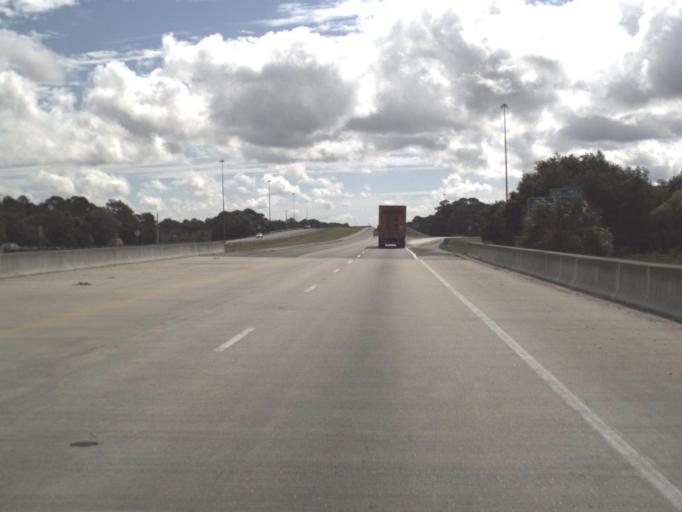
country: US
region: Florida
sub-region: Sarasota County
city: North Port
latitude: 27.0992
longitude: -82.2095
